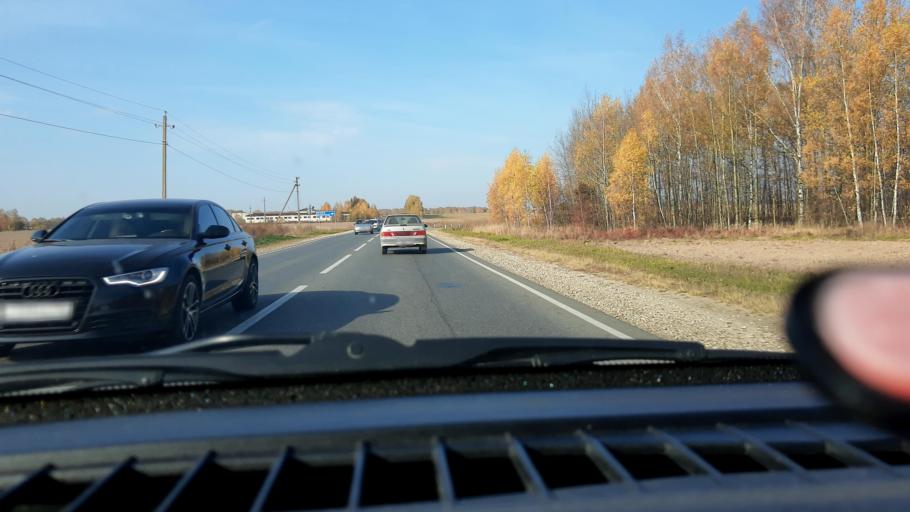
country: RU
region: Nizjnij Novgorod
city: Gorodets
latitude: 56.6208
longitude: 43.5538
